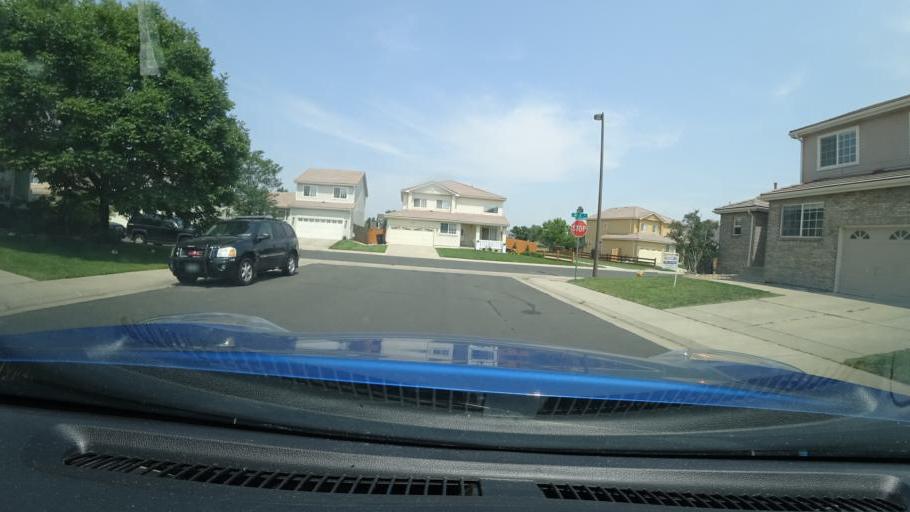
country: US
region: Colorado
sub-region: Adams County
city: Aurora
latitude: 39.7732
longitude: -104.7563
